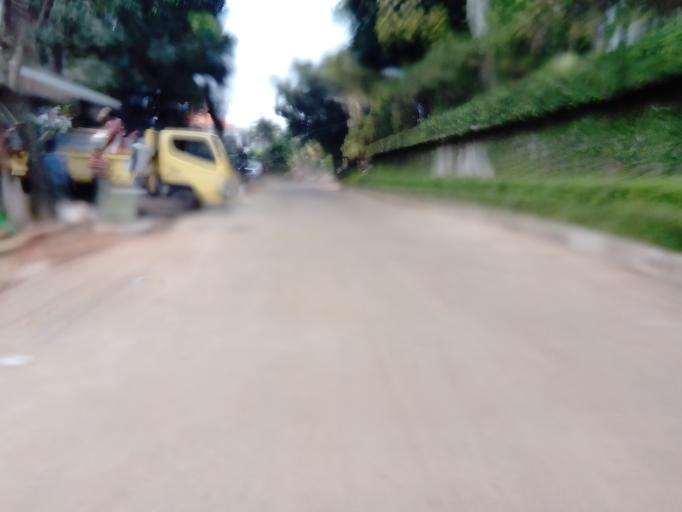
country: ID
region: Jakarta Raya
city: Jakarta
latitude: -6.2250
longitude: 106.7943
